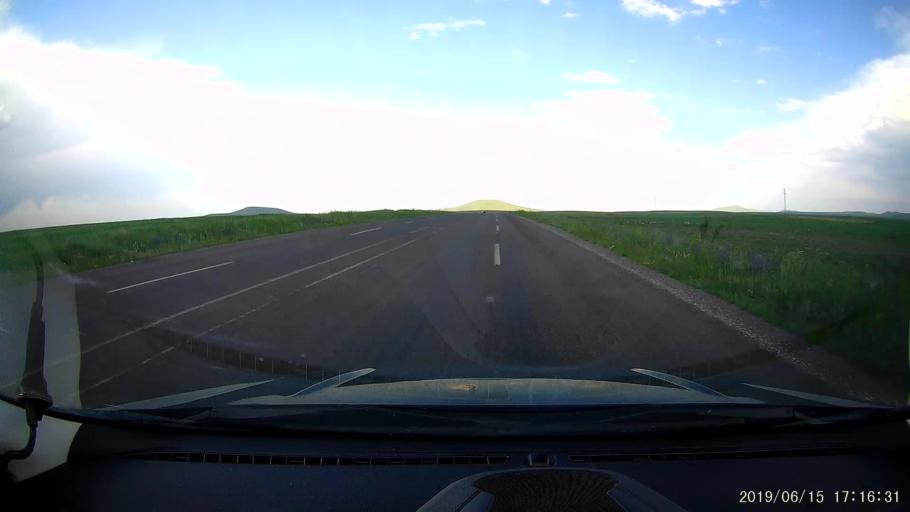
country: TR
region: Kars
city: Kars
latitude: 40.6146
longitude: 43.2193
